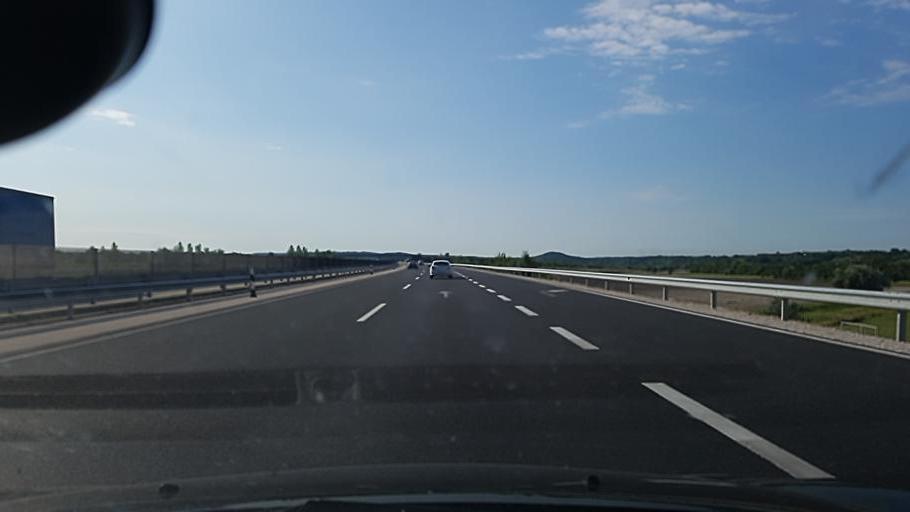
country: HU
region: Fejer
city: Adony
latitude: 47.0951
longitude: 18.8509
